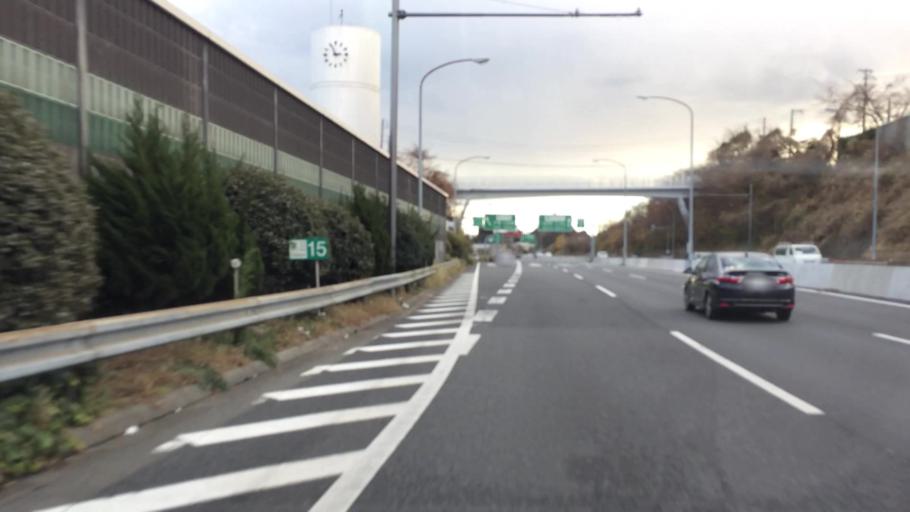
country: JP
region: Kanagawa
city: Yokohama
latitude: 35.4824
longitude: 139.5945
